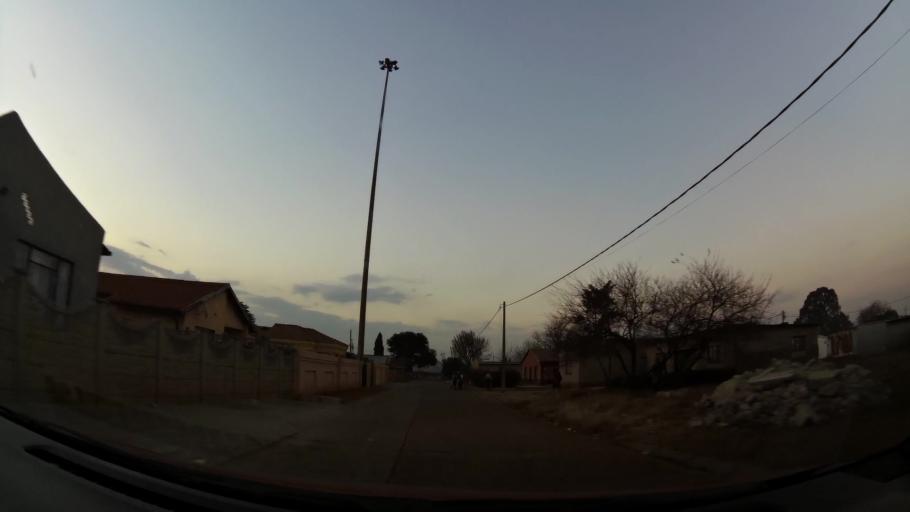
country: ZA
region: Gauteng
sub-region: City of Johannesburg Metropolitan Municipality
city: Orange Farm
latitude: -26.5487
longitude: 27.8490
